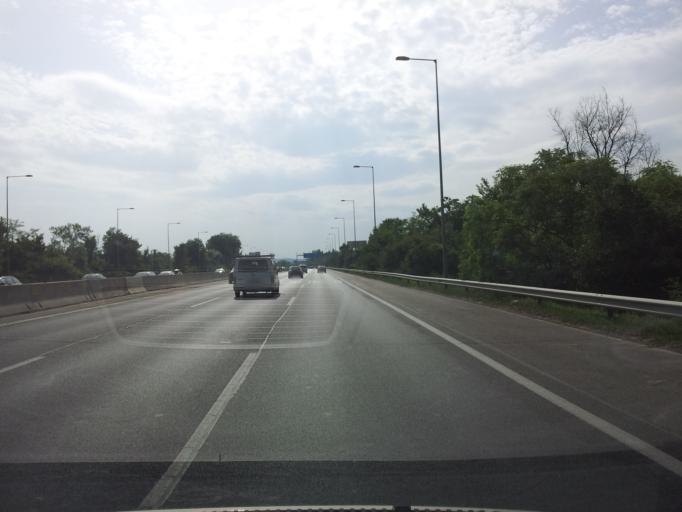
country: HU
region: Pest
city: Budaors
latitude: 47.4522
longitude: 18.9350
